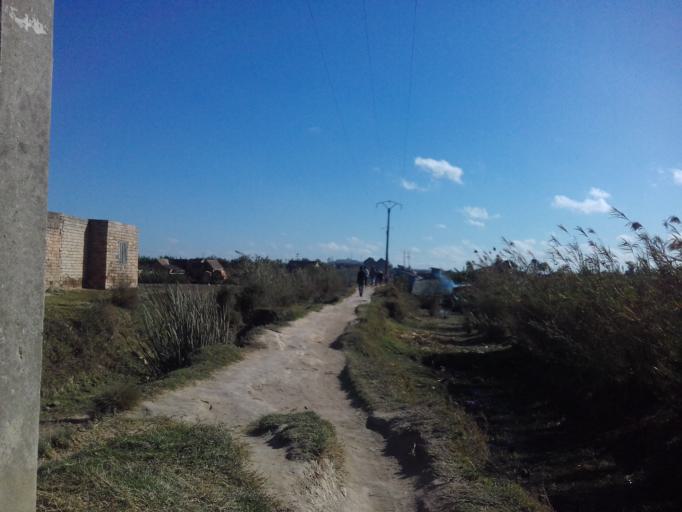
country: MG
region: Analamanga
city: Antananarivo
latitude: -18.8898
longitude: 47.4856
